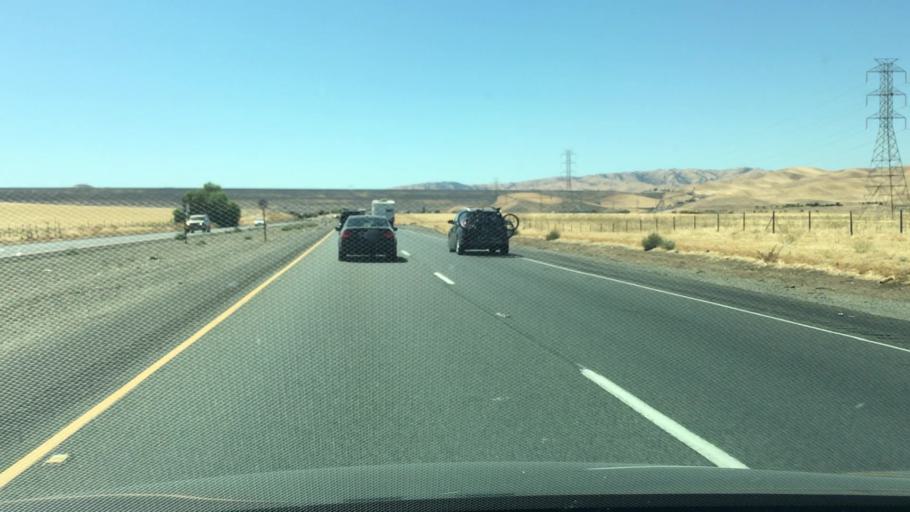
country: US
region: California
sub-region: Merced County
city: Los Banos
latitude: 37.0575
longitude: -121.0439
